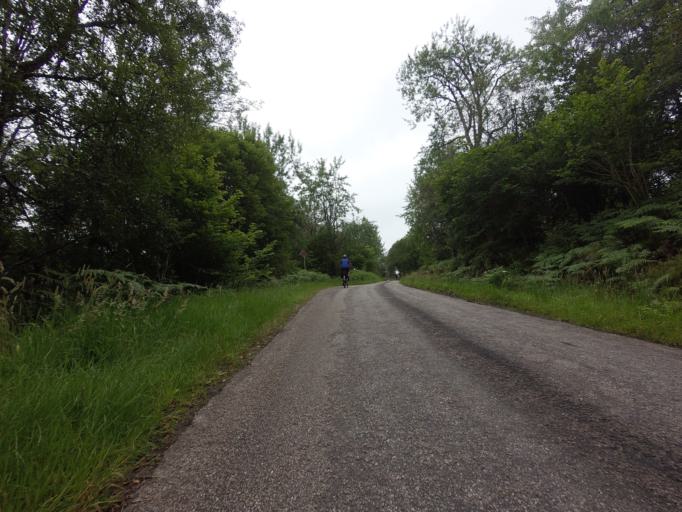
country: GB
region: Scotland
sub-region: Highland
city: Evanton
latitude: 57.9621
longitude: -4.4081
